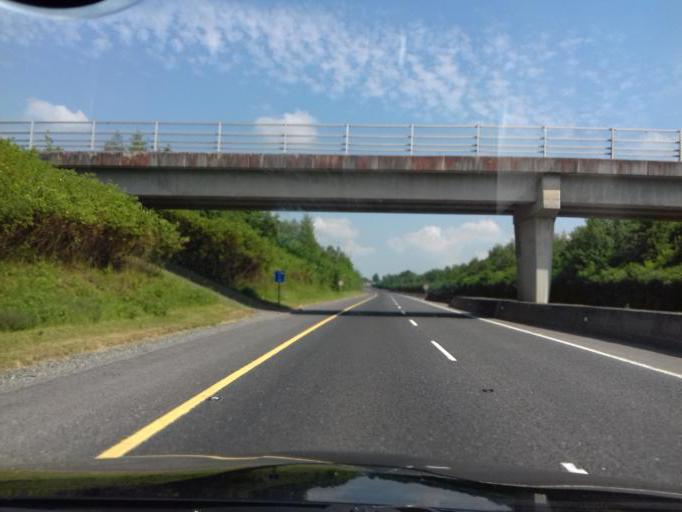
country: IE
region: Leinster
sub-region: An Mhi
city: Ashbourne
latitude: 53.5168
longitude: -6.4200
